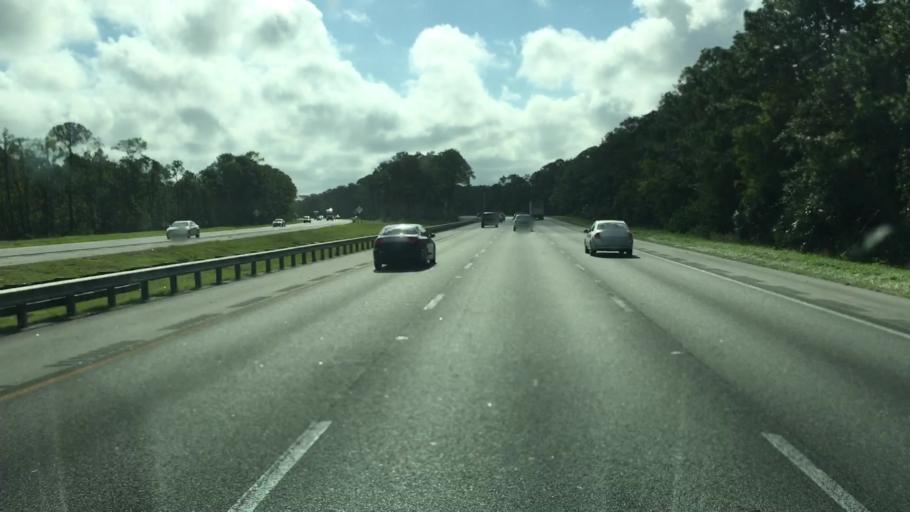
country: US
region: Florida
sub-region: Volusia County
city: South Daytona
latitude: 29.1343
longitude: -81.0637
